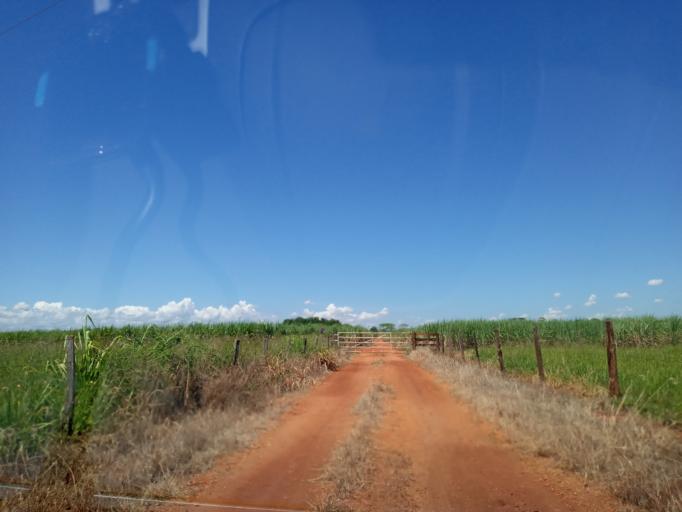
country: BR
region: Goias
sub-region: Itumbiara
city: Itumbiara
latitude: -18.4020
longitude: -49.1215
